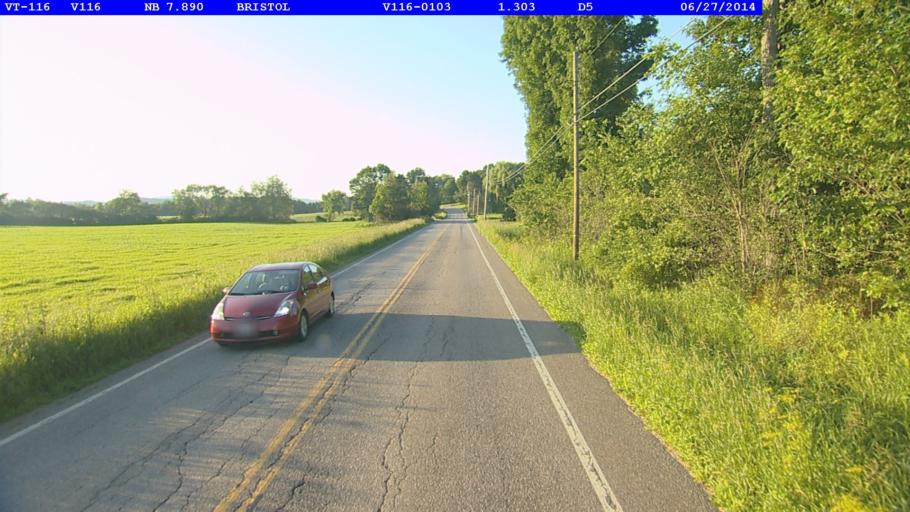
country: US
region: Vermont
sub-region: Addison County
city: Bristol
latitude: 44.0725
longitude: -73.0858
